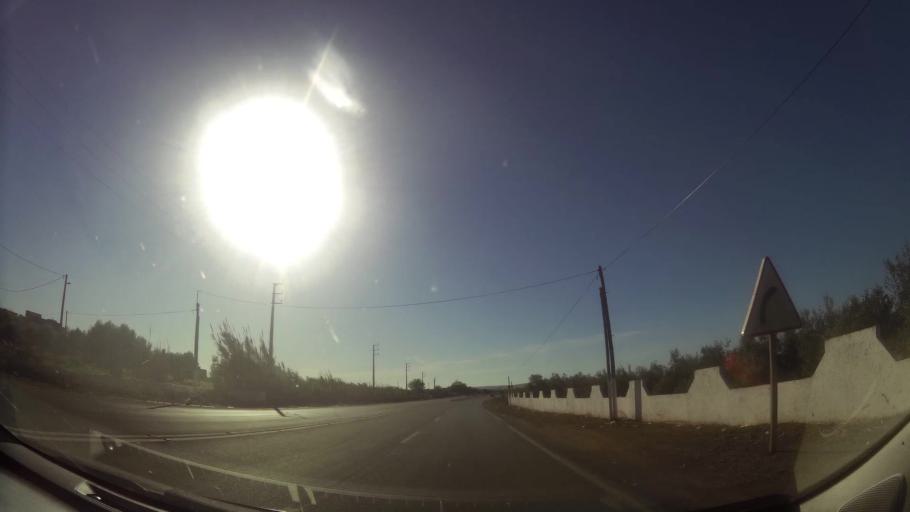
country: MA
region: Oriental
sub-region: Berkane-Taourirt
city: Ahfir
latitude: 35.0104
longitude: -2.1946
